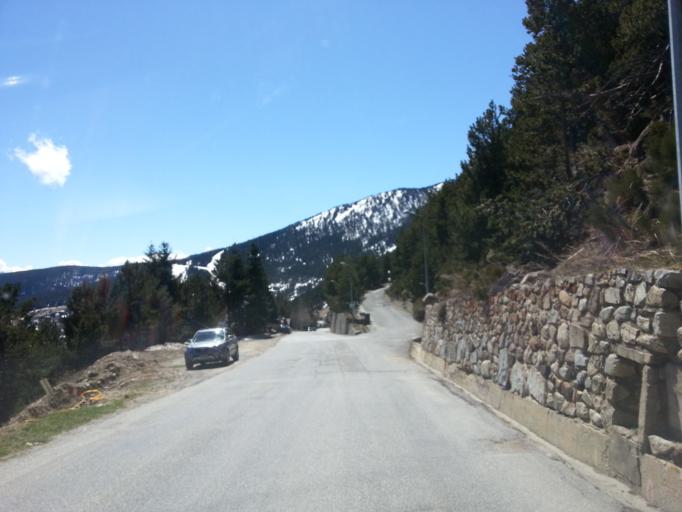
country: ES
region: Catalonia
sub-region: Provincia de Girona
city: Llivia
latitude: 42.5866
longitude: 2.0756
